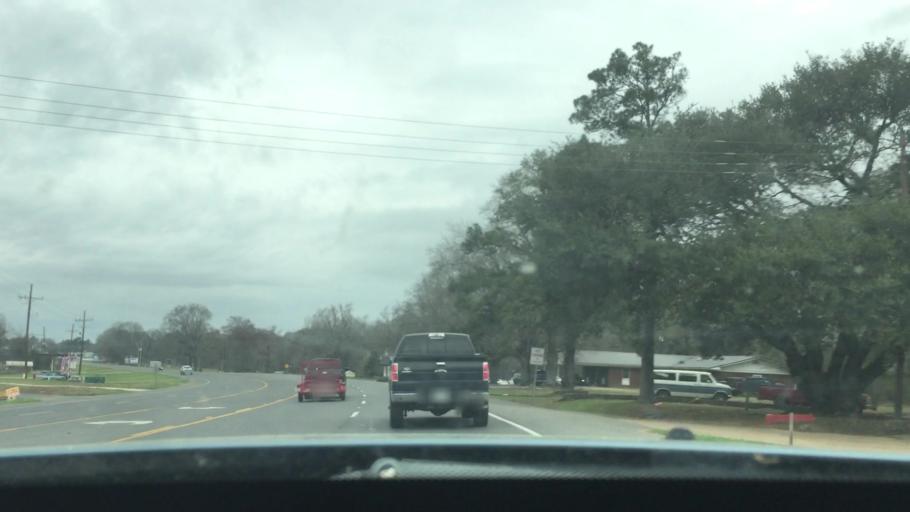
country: US
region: Louisiana
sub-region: Franklin Parish
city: Winnsboro
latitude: 32.1520
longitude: -91.7069
